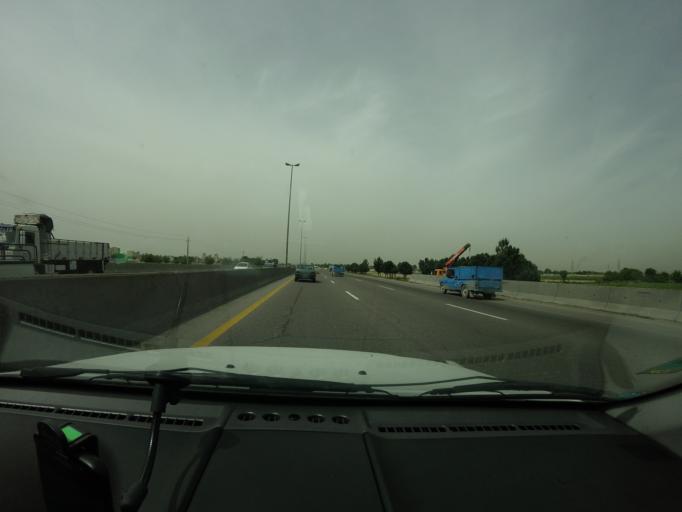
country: IR
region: Tehran
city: Eslamshahr
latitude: 35.5767
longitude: 51.1489
